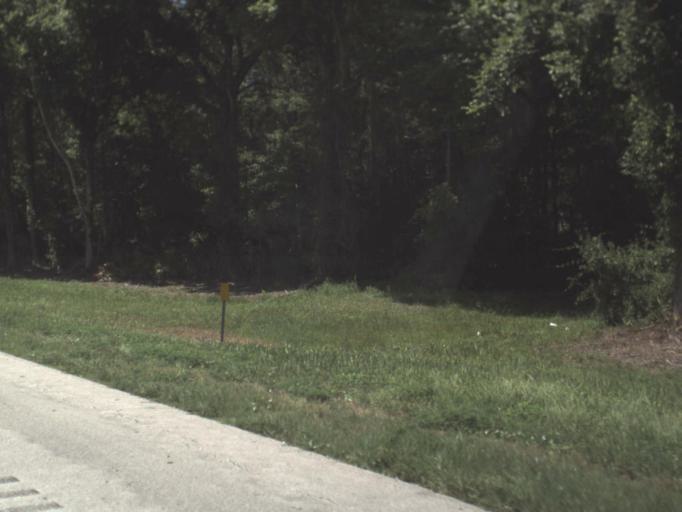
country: US
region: Florida
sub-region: Saint Johns County
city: Saint Augustine
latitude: 29.8871
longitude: -81.4030
